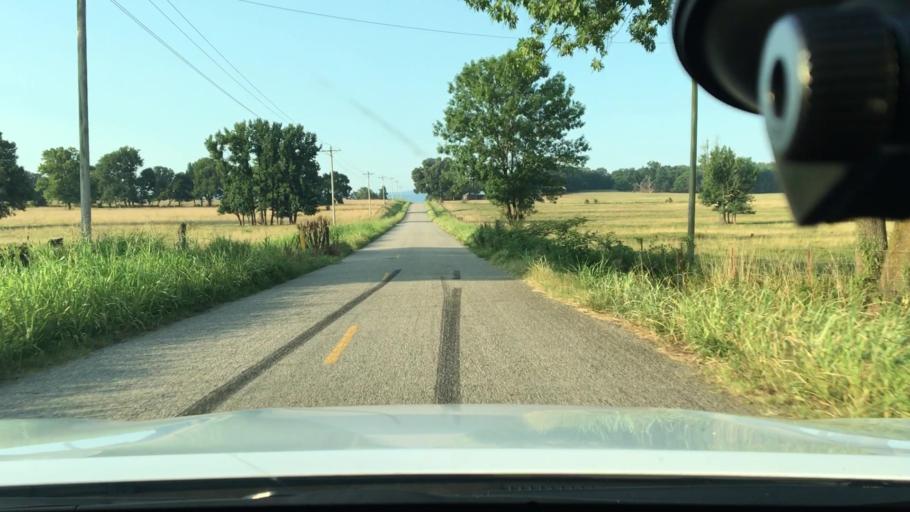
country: US
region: Arkansas
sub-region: Johnson County
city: Coal Hill
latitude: 35.3551
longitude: -93.6133
